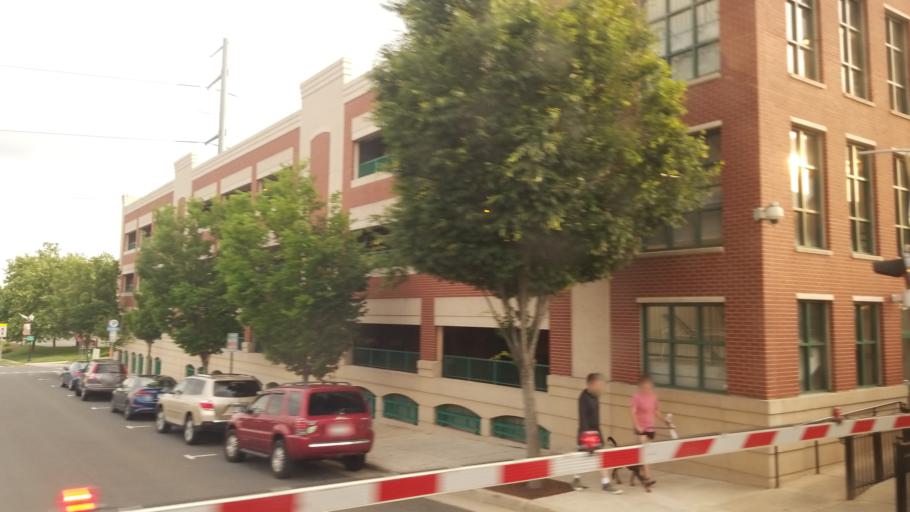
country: US
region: Virginia
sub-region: City of Manassas
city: Manassas
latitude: 38.7504
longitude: -77.4714
